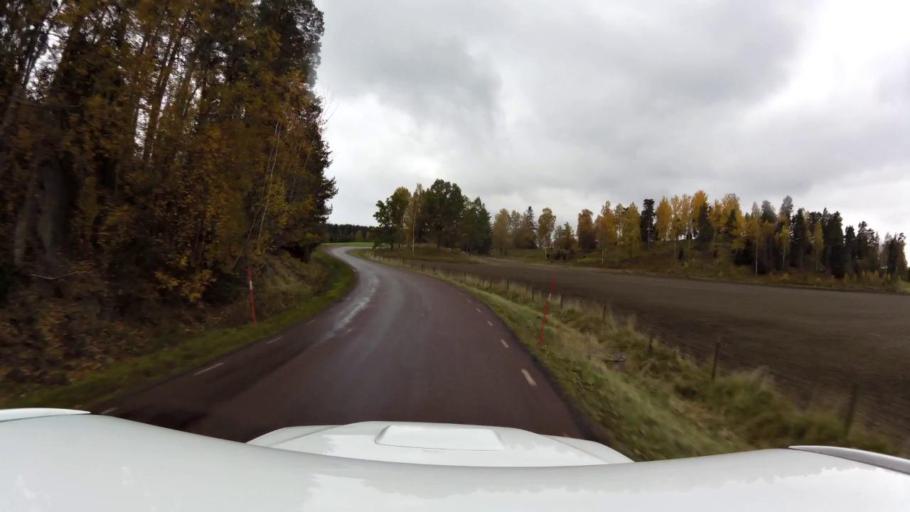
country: SE
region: OEstergoetland
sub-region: Linkopings Kommun
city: Ljungsbro
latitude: 58.5361
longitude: 15.5244
